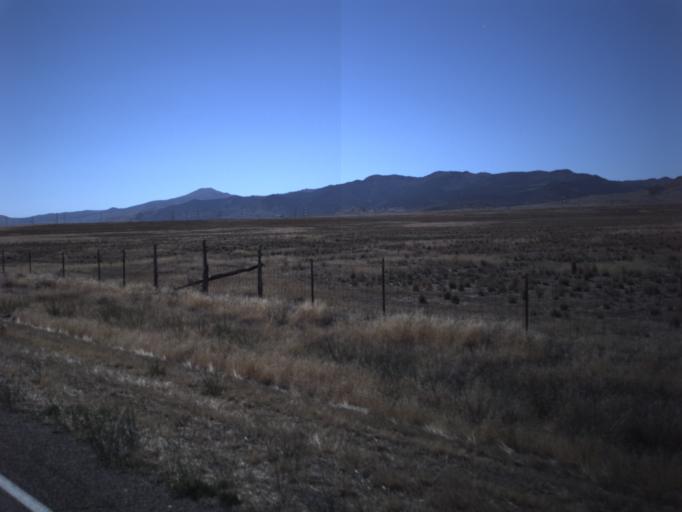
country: US
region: Utah
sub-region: Utah County
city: Genola
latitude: 39.9886
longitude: -111.9574
